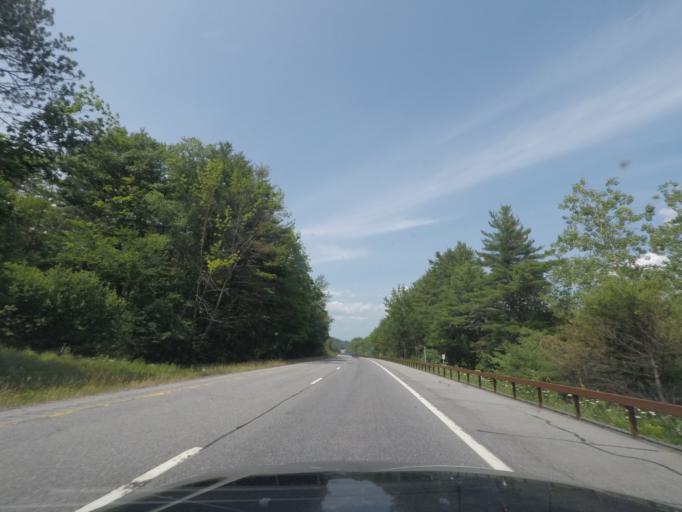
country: US
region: New York
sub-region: Warren County
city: Warrensburg
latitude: 43.7678
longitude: -73.8025
